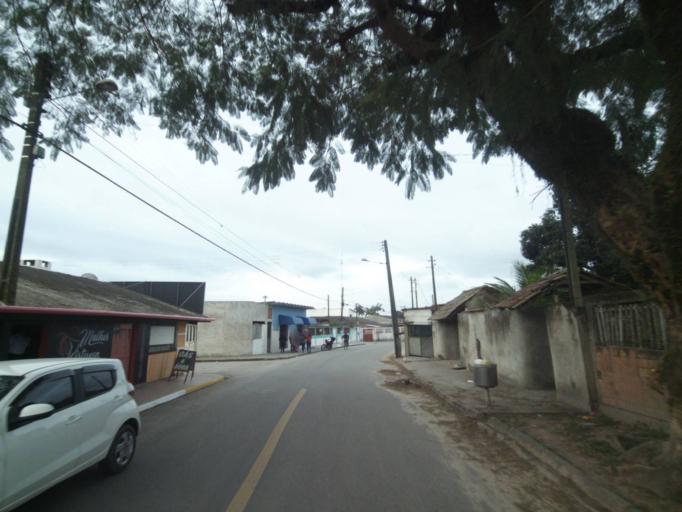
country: BR
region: Parana
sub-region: Paranagua
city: Paranagua
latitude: -25.5336
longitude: -48.5462
